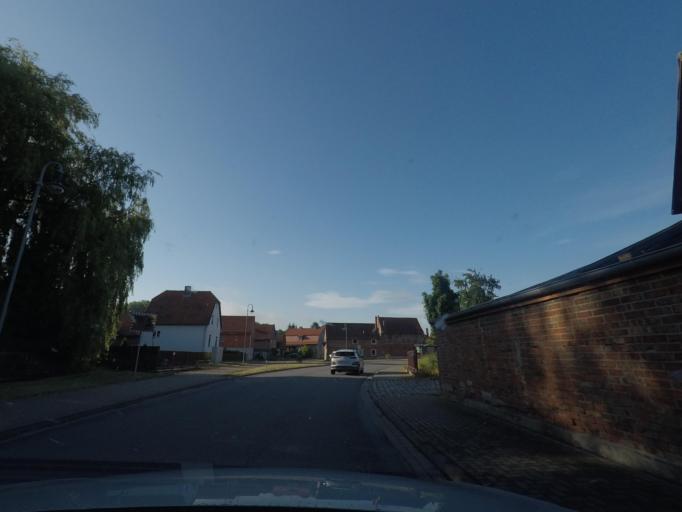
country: DE
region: Saxony-Anhalt
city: Huy-Neinstedt
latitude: 52.0156
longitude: 10.8985
